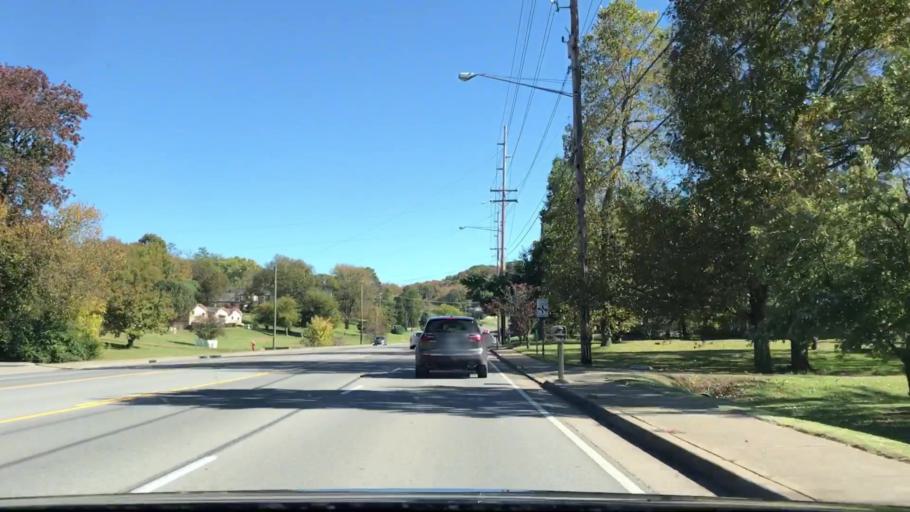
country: US
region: Tennessee
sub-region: Williamson County
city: Brentwood Estates
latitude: 36.0396
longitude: -86.7388
